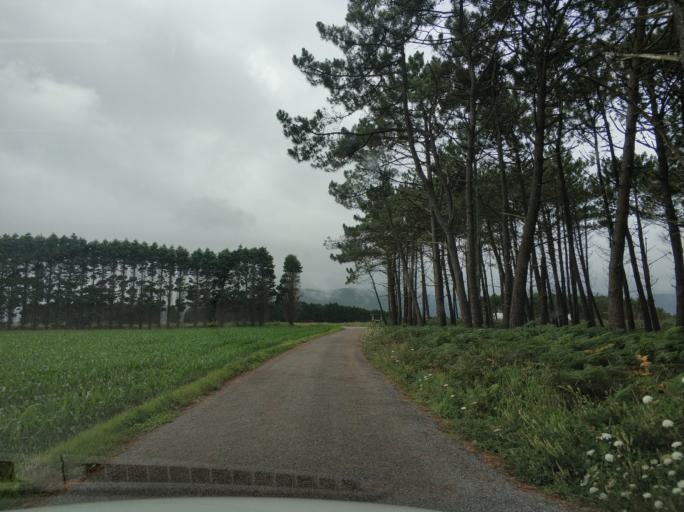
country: ES
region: Asturias
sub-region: Province of Asturias
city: Tineo
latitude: 43.5655
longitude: -6.4702
